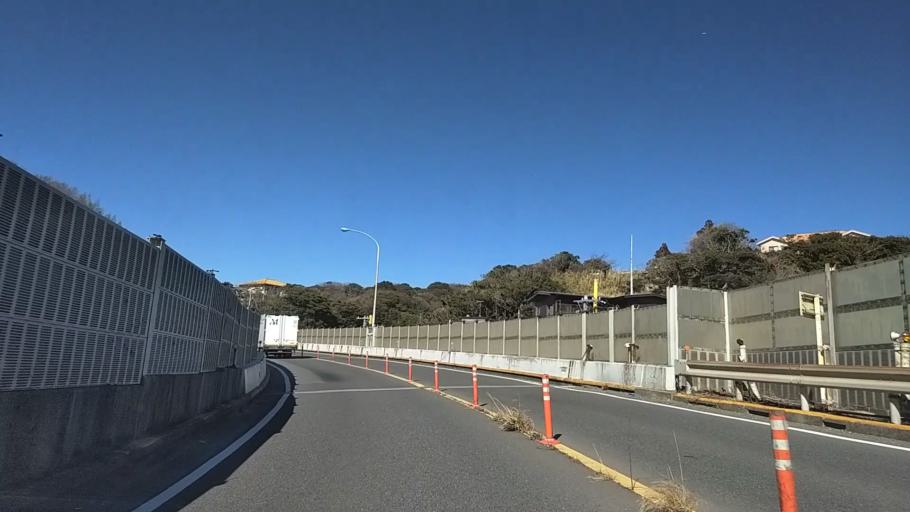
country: JP
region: Kanagawa
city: Kamakura
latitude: 35.2980
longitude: 139.5582
